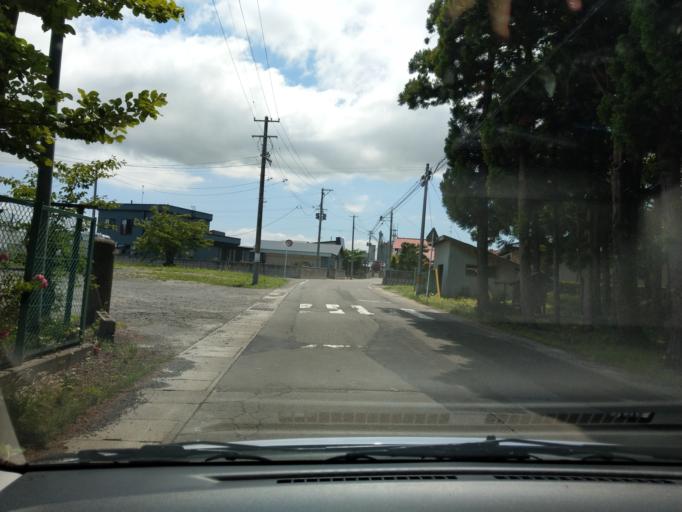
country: JP
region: Aomori
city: Kuroishi
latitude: 40.6774
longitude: 140.5594
